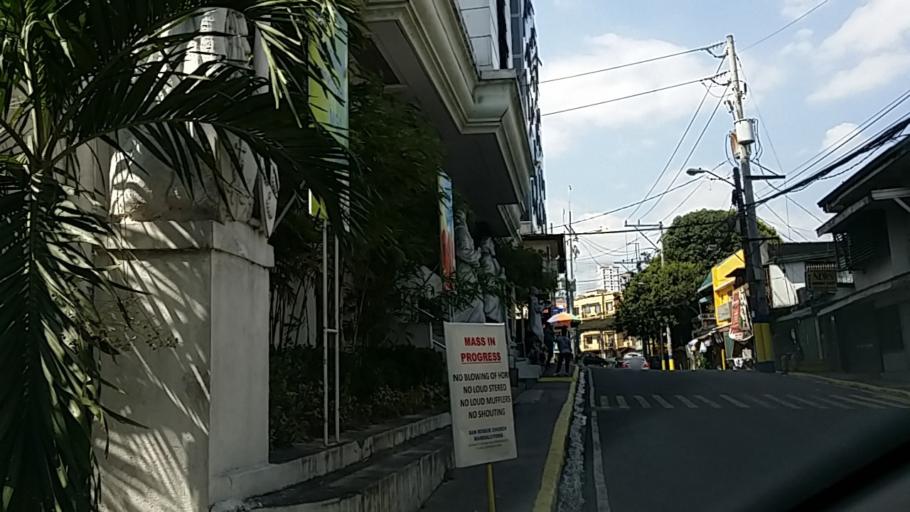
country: PH
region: Metro Manila
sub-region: Mandaluyong
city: Mandaluyong City
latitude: 14.5724
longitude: 121.0448
